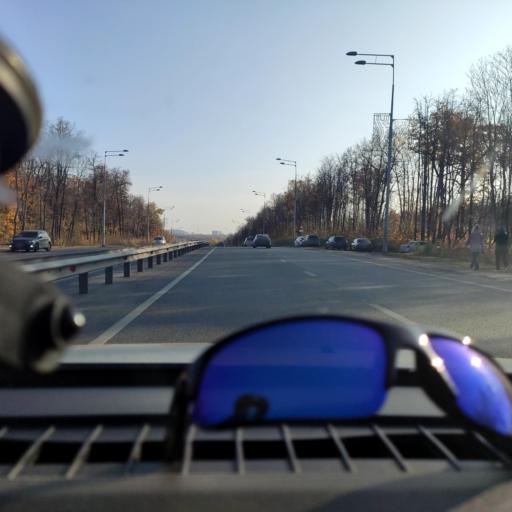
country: RU
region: Samara
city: Novosemeykino
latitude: 53.3181
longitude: 50.2301
